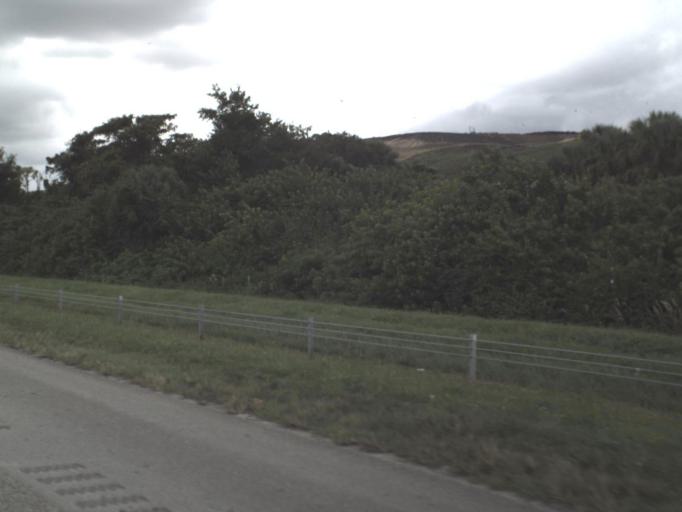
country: US
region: Florida
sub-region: Palm Beach County
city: Palm Beach Gardens
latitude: 26.7700
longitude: -80.1333
